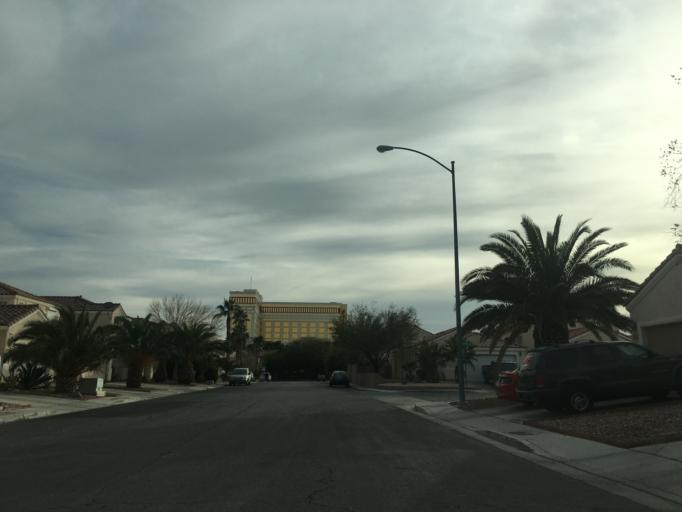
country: US
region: Nevada
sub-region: Clark County
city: Enterprise
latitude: 36.0169
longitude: -115.1770
